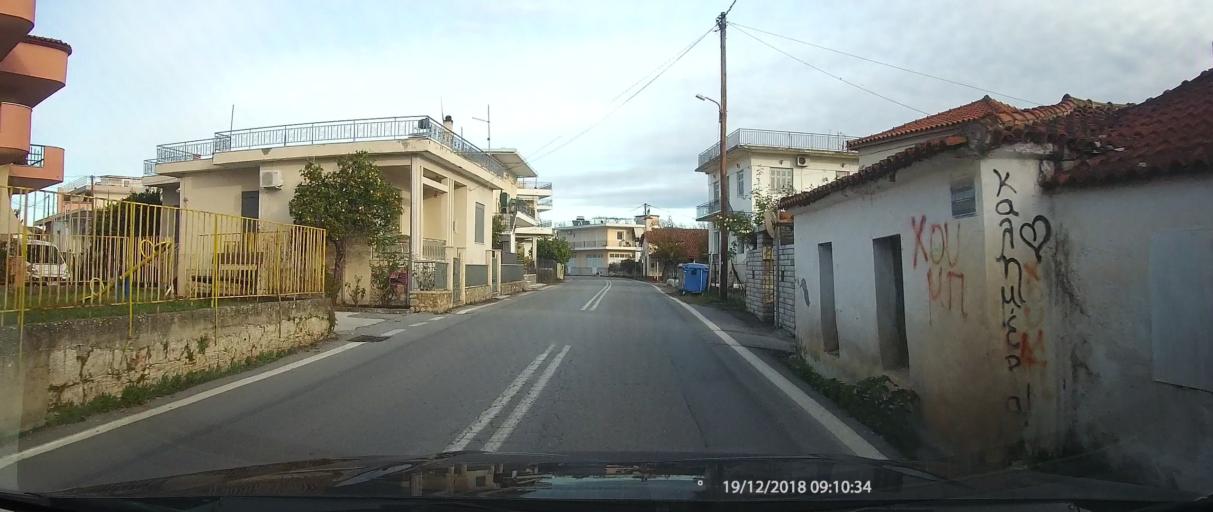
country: GR
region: Peloponnese
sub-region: Nomos Lakonias
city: Sparti
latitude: 37.0754
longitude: 22.4200
